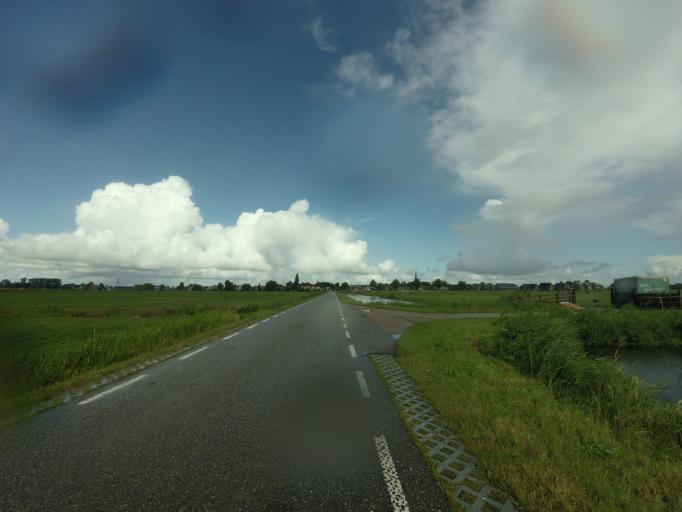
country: NL
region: Friesland
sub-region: Gemeente Leeuwarden
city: Wirdum
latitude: 53.1438
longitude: 5.8035
